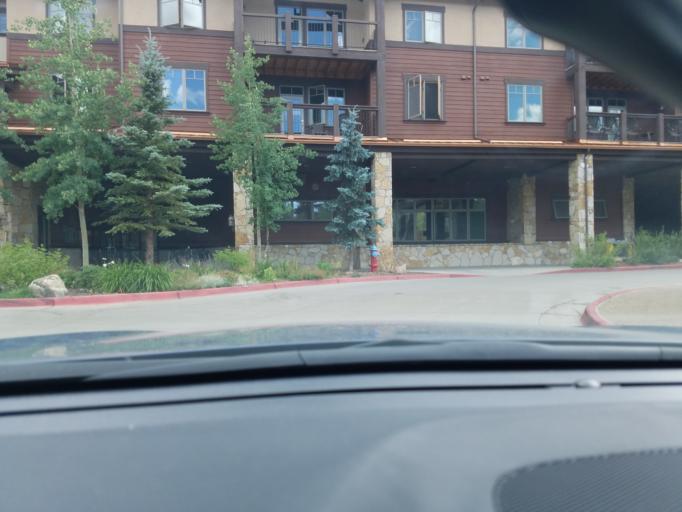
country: US
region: Colorado
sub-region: Summit County
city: Breckenridge
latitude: 39.4758
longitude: -106.0530
